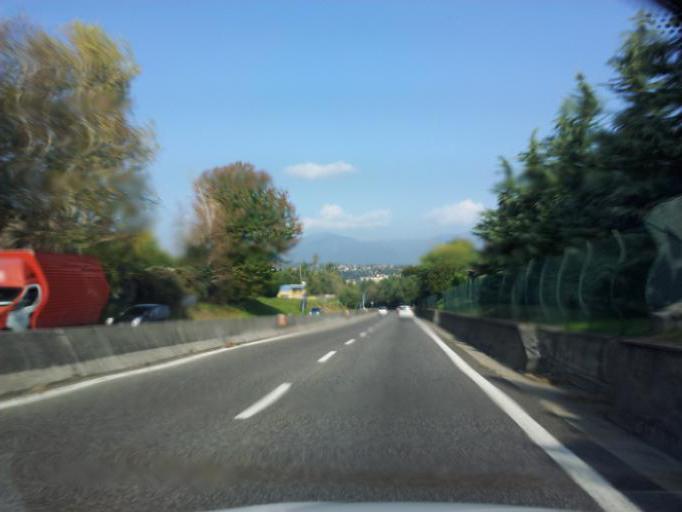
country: IT
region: Lombardy
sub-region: Provincia di Varese
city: Malgesso
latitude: 45.8282
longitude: 8.6704
